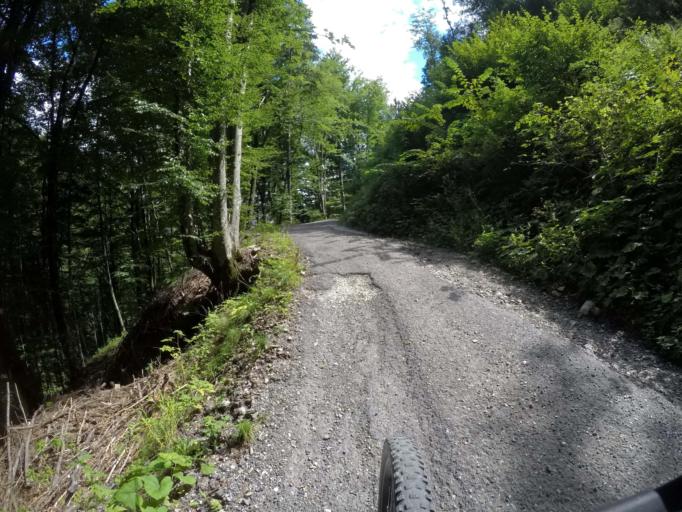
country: IT
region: Friuli Venezia Giulia
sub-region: Provincia di Udine
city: Arta Terme
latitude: 46.4842
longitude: 13.0637
